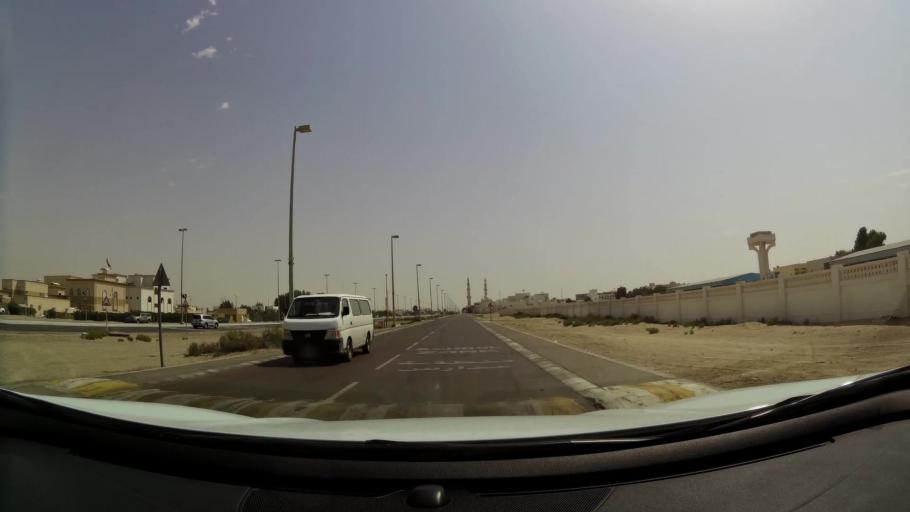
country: AE
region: Abu Dhabi
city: Abu Dhabi
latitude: 24.3042
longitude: 54.6421
